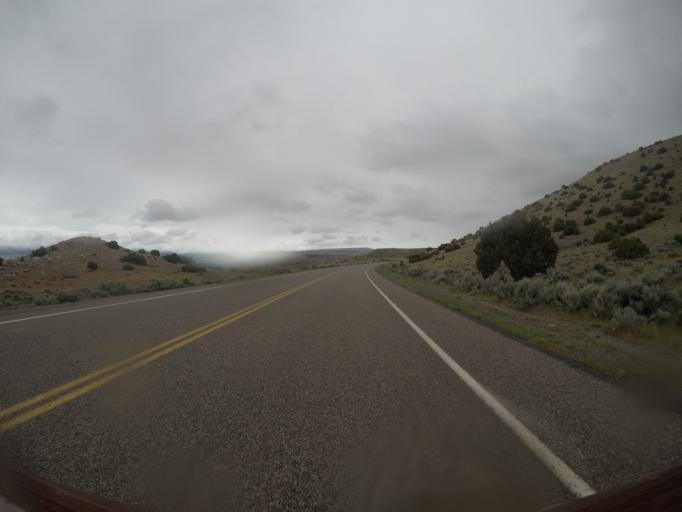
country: US
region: Wyoming
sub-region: Big Horn County
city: Lovell
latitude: 45.0730
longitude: -108.2562
